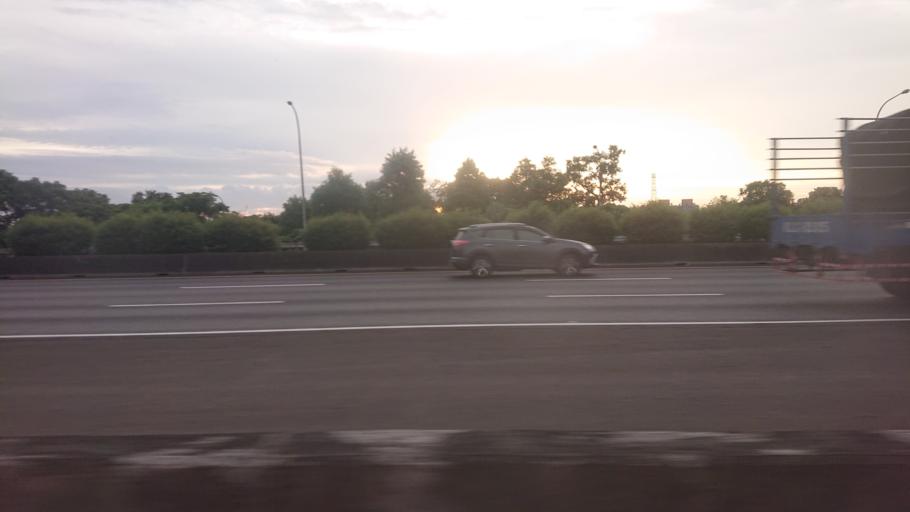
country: TW
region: Taiwan
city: Daxi
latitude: 24.8940
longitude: 121.2657
